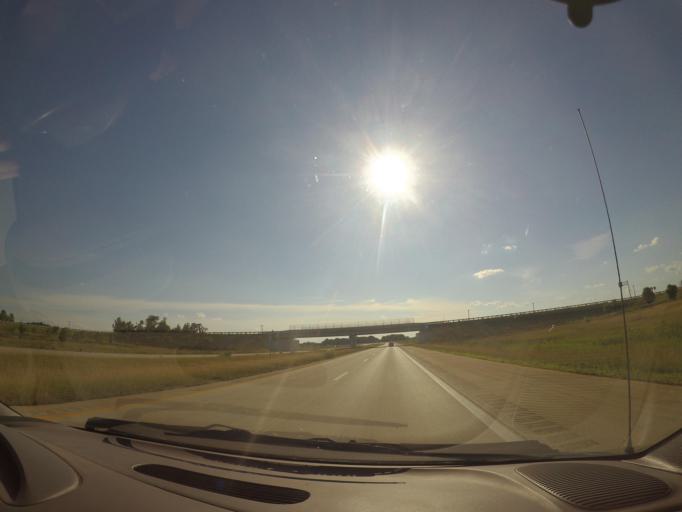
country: US
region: Ohio
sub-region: Lucas County
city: Whitehouse
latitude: 41.4559
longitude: -83.8243
